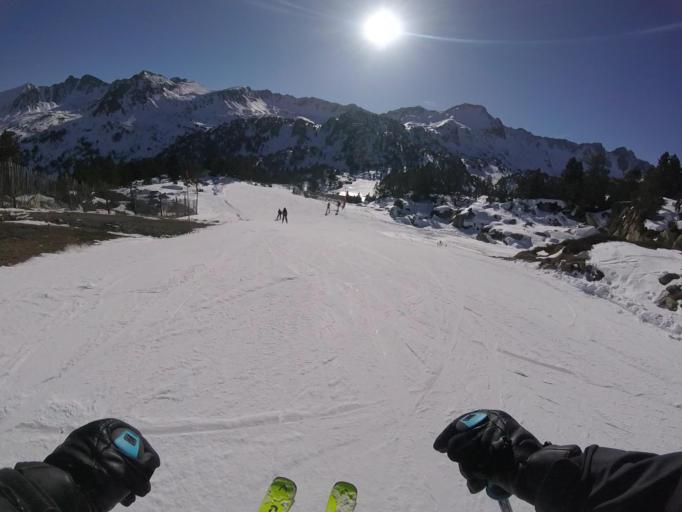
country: AD
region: Encamp
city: Pas de la Casa
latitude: 42.5278
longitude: 1.6871
